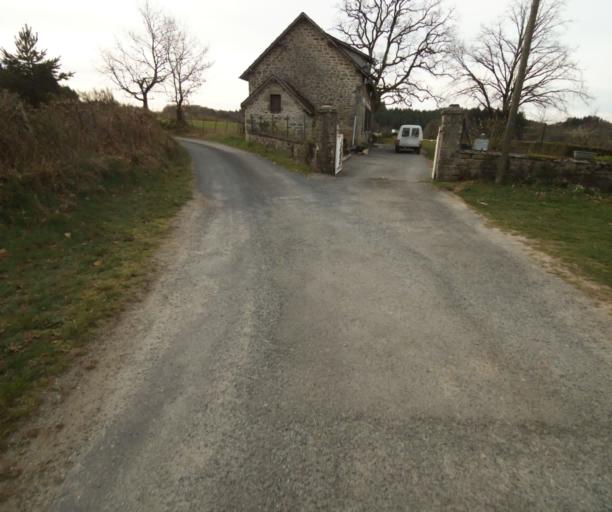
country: FR
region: Limousin
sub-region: Departement de la Correze
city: Treignac
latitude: 45.4546
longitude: 1.8213
